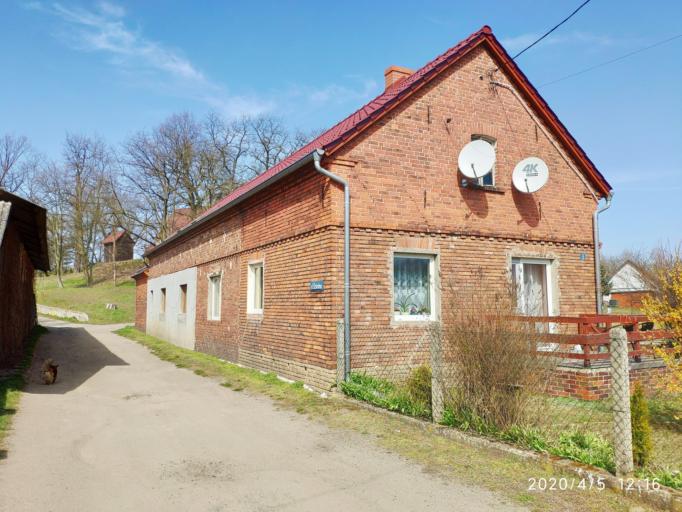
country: PL
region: Lubusz
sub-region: Powiat krosnienski
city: Dabie
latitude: 52.0279
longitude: 15.2481
